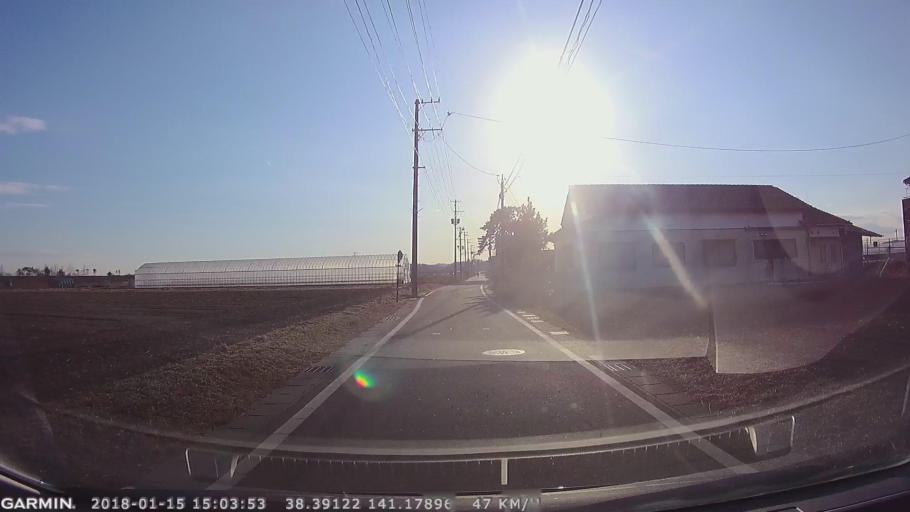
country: JP
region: Miyagi
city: Yamoto
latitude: 38.3913
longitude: 141.1791
